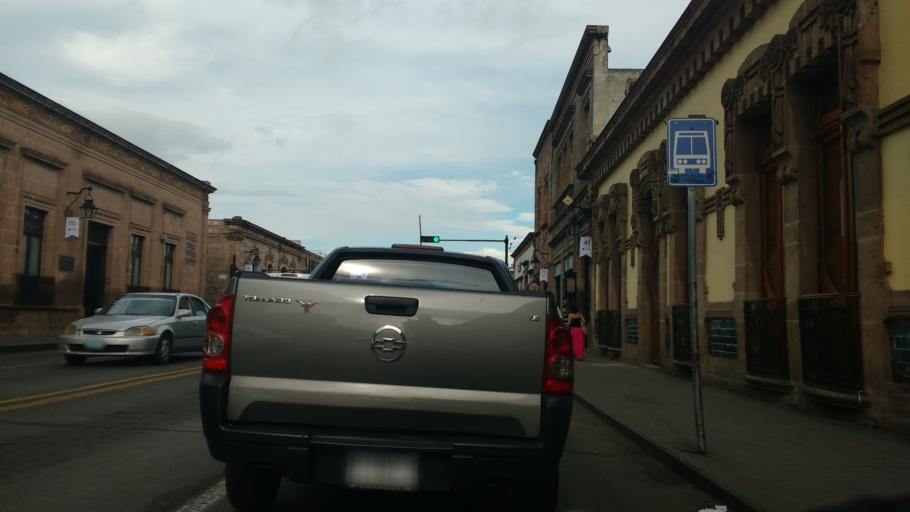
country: MX
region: Michoacan
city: Morelia
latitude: 19.7029
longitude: -101.1846
